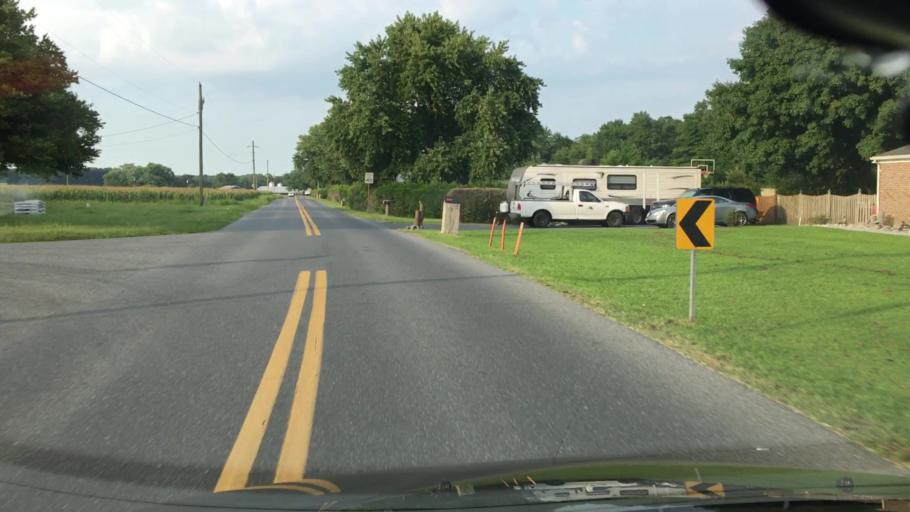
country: US
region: Delaware
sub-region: Sussex County
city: Selbyville
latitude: 38.4570
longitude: -75.1807
